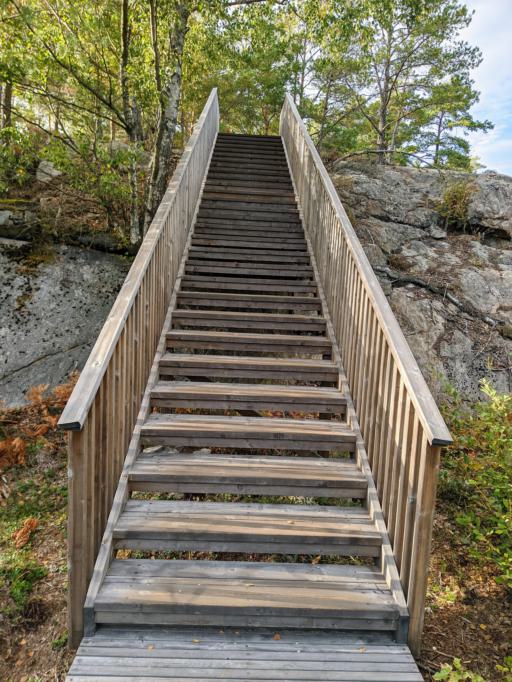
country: SE
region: Vaestra Goetaland
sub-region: Tanums Kommun
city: Tanumshede
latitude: 58.7020
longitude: 11.3332
